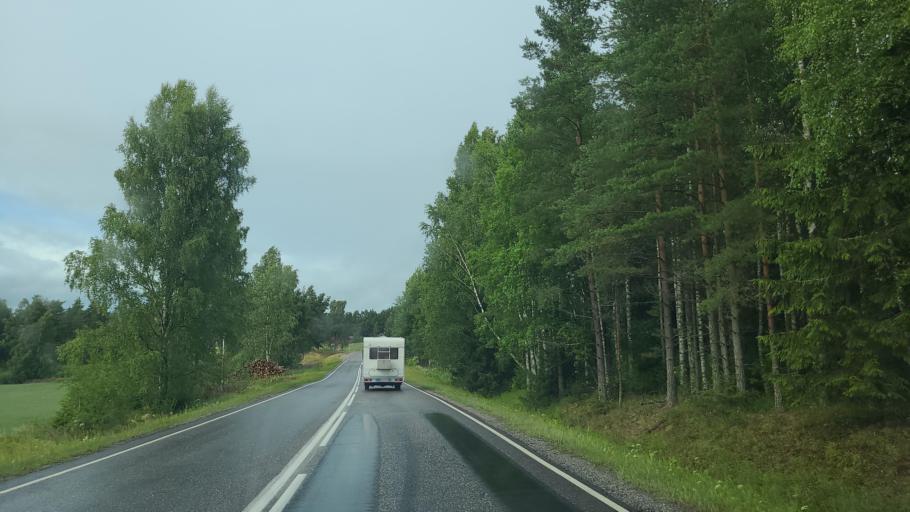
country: FI
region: Varsinais-Suomi
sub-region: Turku
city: Sauvo
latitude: 60.3072
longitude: 22.6872
